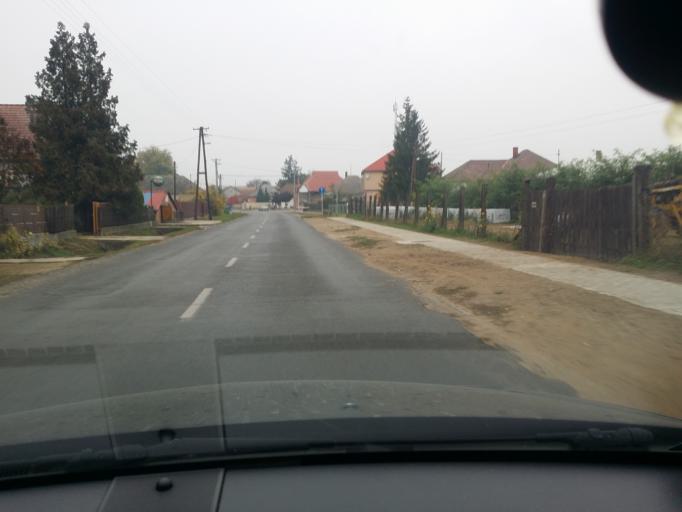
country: HU
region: Szabolcs-Szatmar-Bereg
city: Kek
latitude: 48.1139
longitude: 21.8797
